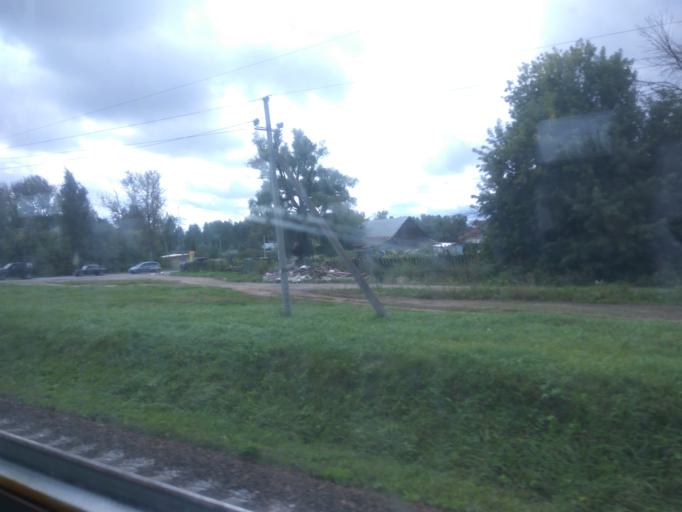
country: RU
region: Moskovskaya
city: Beloozerskiy
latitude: 55.4755
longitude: 38.4198
